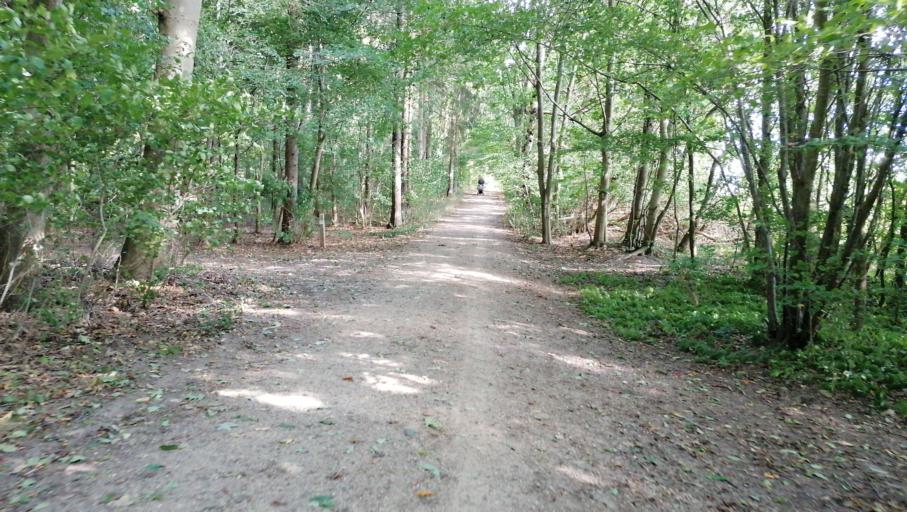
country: DK
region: Zealand
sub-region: Holbaek Kommune
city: Holbaek
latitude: 55.7085
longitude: 11.6900
